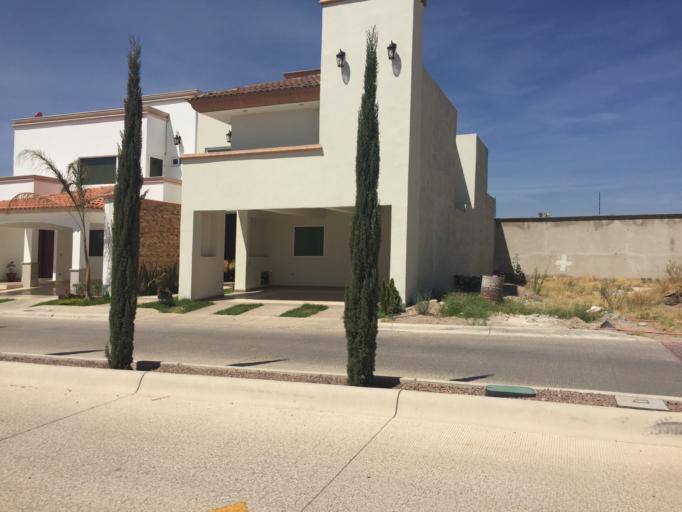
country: MX
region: Durango
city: Victoria de Durango
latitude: 24.0001
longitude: -104.6393
